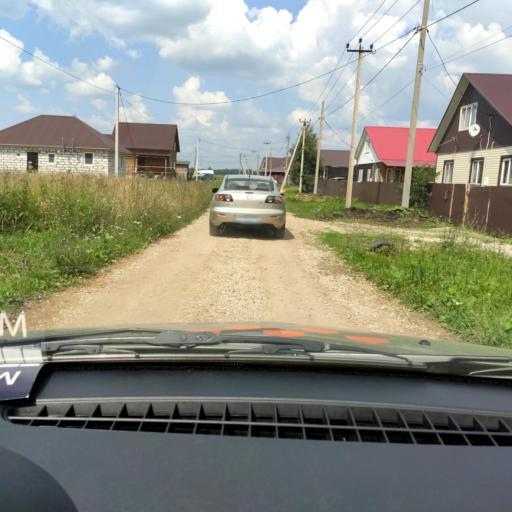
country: RU
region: Bashkortostan
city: Iglino
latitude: 54.8275
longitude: 56.3729
